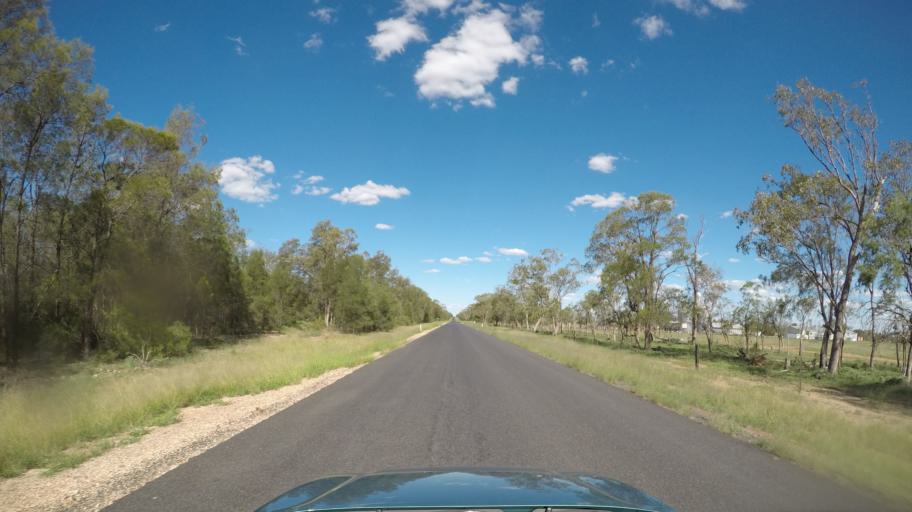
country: AU
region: Queensland
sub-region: Goondiwindi
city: Goondiwindi
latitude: -28.1484
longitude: 150.3139
